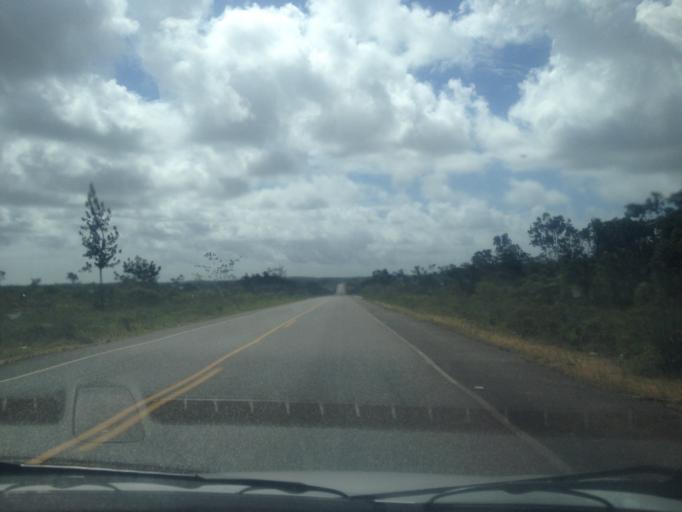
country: BR
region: Bahia
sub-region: Entre Rios
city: Entre Rios
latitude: -12.2622
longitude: -37.8704
